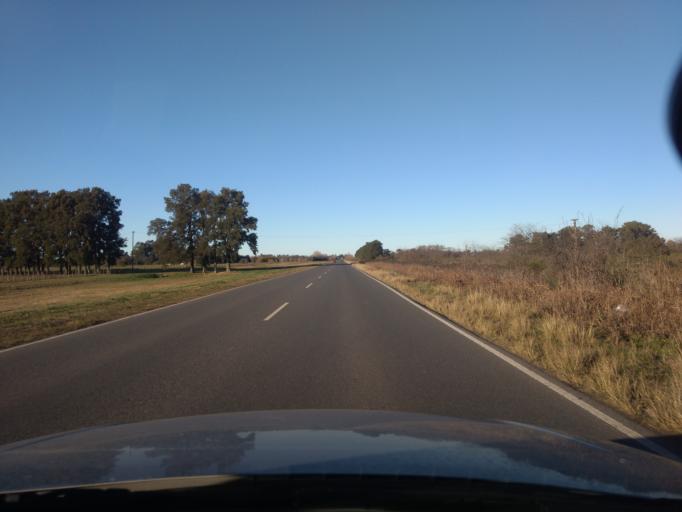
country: AR
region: Buenos Aires
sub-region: Partido de Lujan
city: Lujan
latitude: -34.6054
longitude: -59.1054
